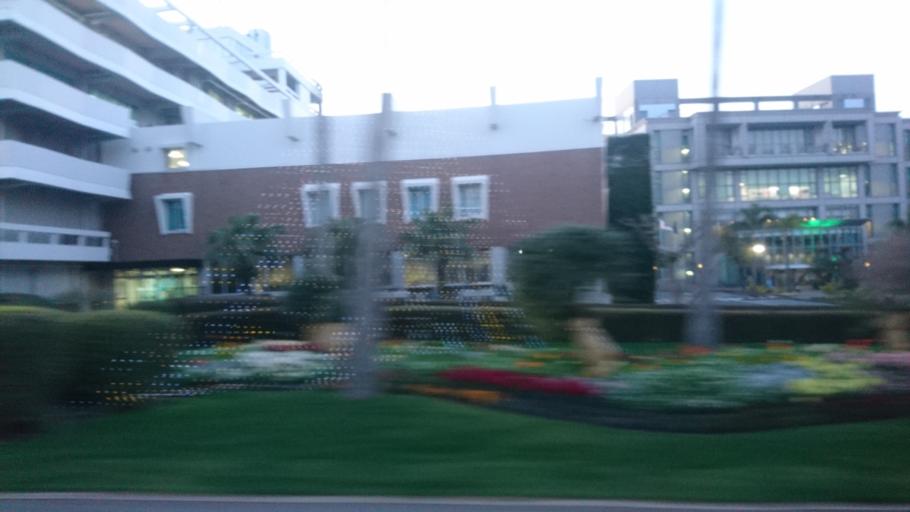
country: JP
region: Miyazaki
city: Miyazaki-shi
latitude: 31.9077
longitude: 131.4211
